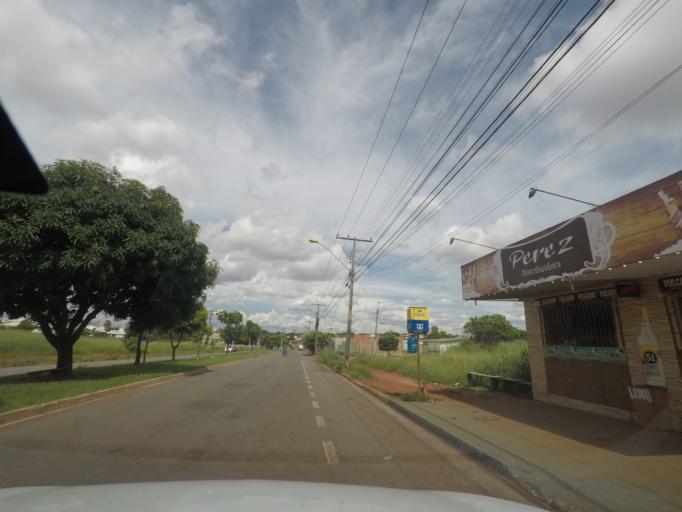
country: BR
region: Goias
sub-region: Goiania
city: Goiania
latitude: -16.7189
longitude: -49.3298
